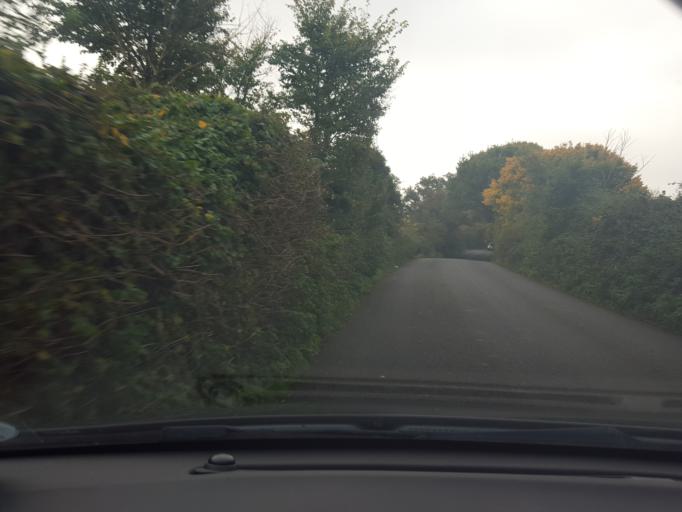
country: GB
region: England
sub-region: Essex
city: Saint Osyth
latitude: 51.7936
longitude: 1.0862
